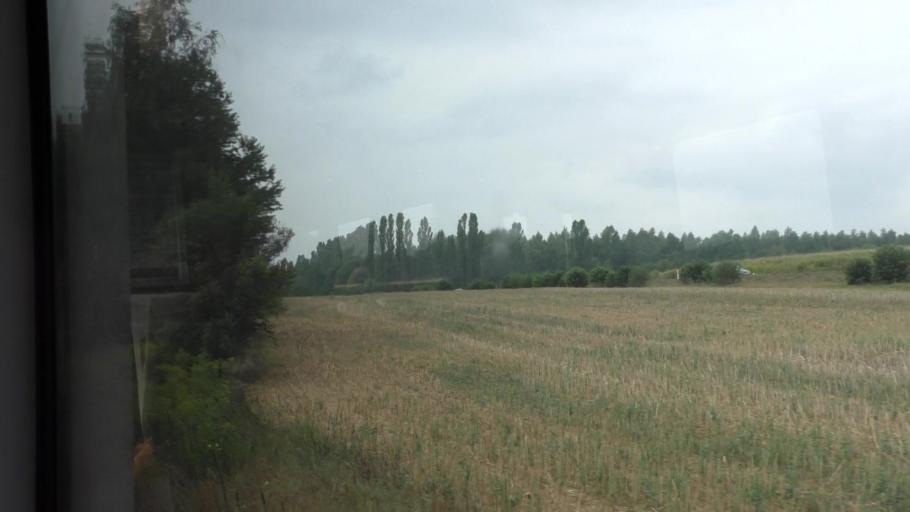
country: DE
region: Saxony
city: Hirschfelde
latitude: 50.9333
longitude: 14.8741
